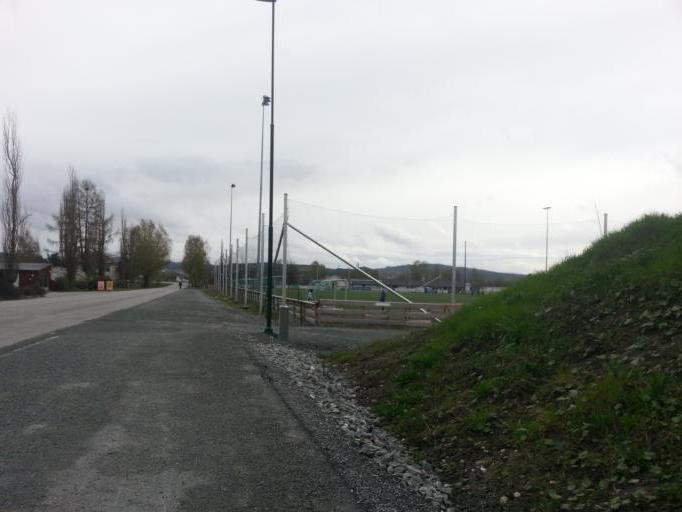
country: NO
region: Nord-Trondelag
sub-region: Levanger
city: Skogn
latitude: 63.7016
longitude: 11.1946
